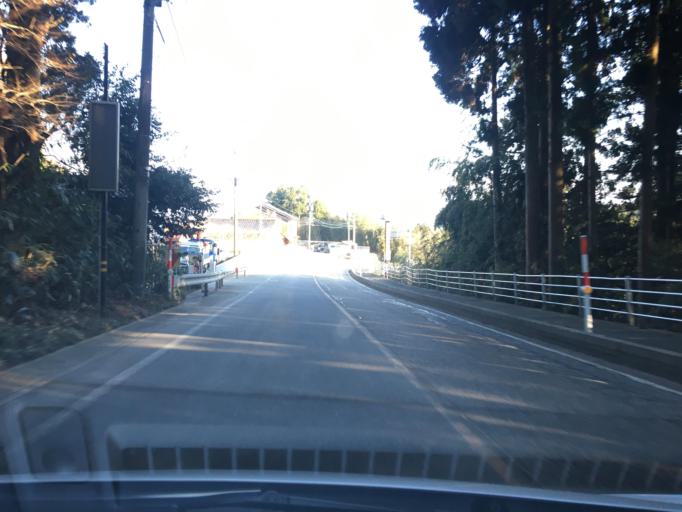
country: JP
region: Ishikawa
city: Nanao
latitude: 36.9807
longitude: 137.0498
